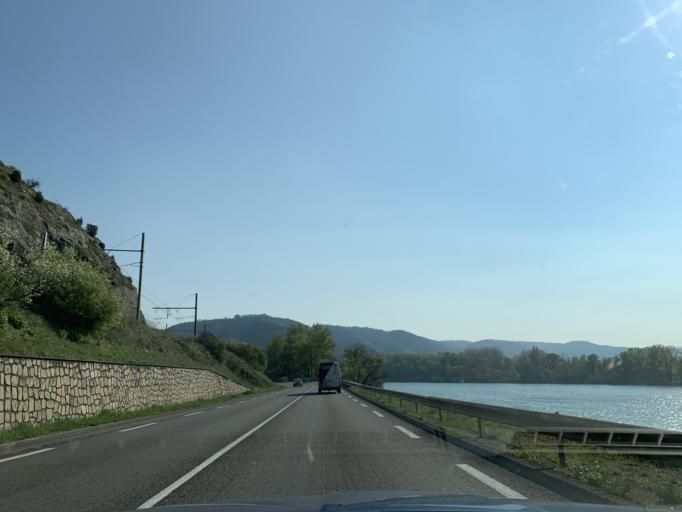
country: FR
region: Rhone-Alpes
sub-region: Departement de l'Ardeche
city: Tournon-sur-Rhone
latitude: 45.0826
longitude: 4.8308
